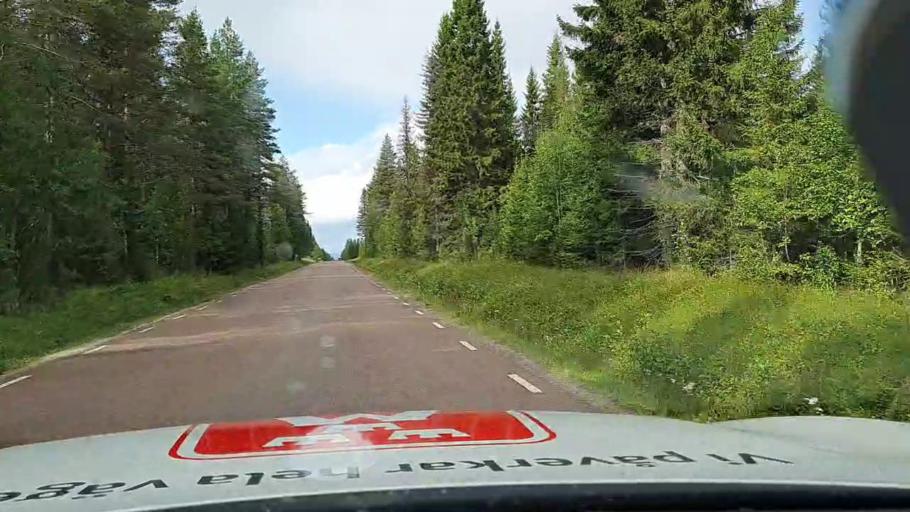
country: SE
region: Jaemtland
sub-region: Stroemsunds Kommun
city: Stroemsund
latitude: 63.8690
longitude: 15.3729
